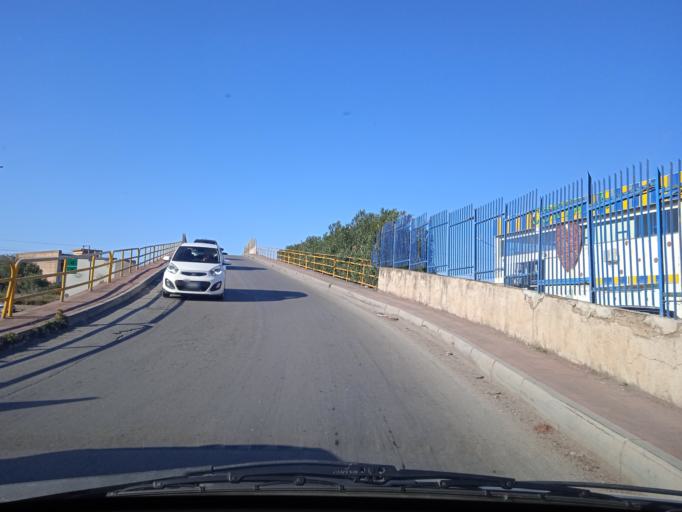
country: IT
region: Sicily
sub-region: Palermo
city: Villabate
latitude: 38.0857
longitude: 13.4499
